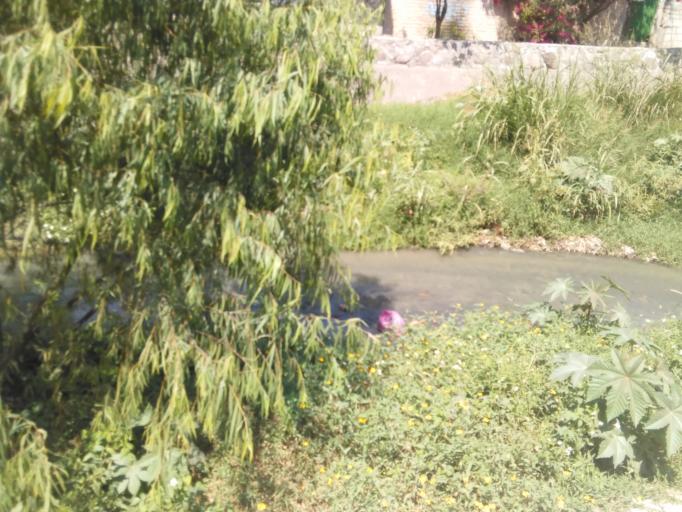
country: MX
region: Nayarit
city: Tepic
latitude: 21.4882
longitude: -104.8751
